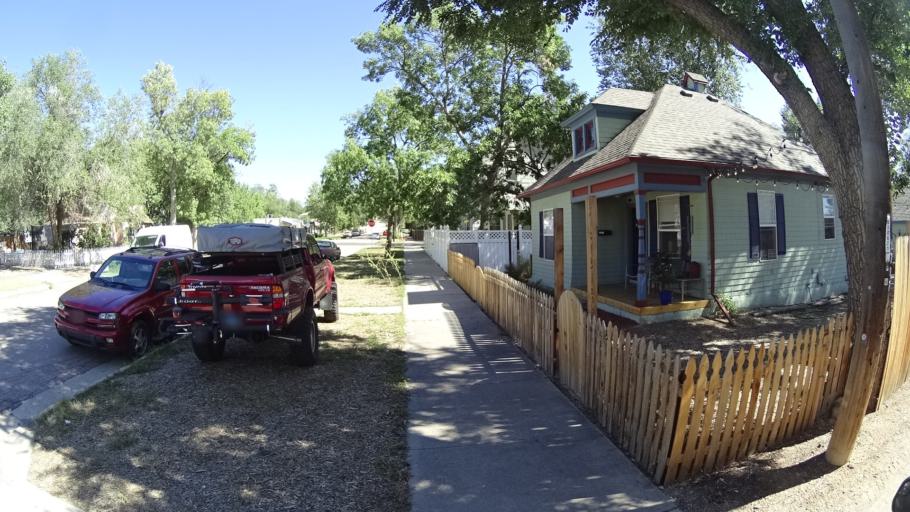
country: US
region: Colorado
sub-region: El Paso County
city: Colorado Springs
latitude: 38.8415
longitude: -104.8520
